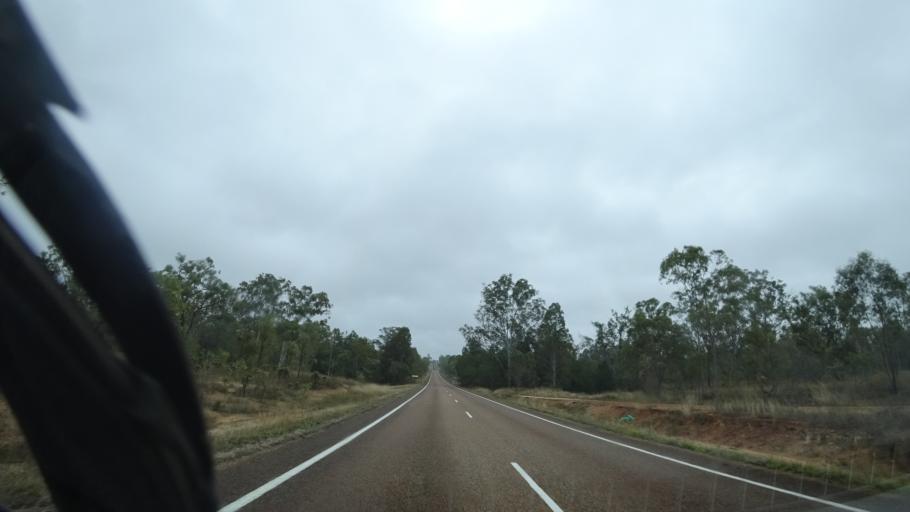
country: AU
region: Queensland
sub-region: Tablelands
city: Ravenshoe
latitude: -17.6912
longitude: 145.1552
